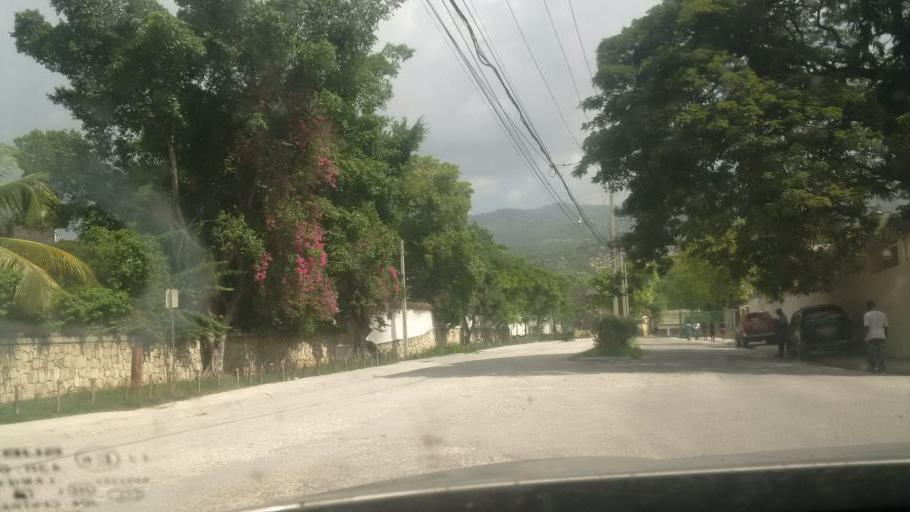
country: HT
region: Ouest
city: Petionville
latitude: 18.5234
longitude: -72.2551
